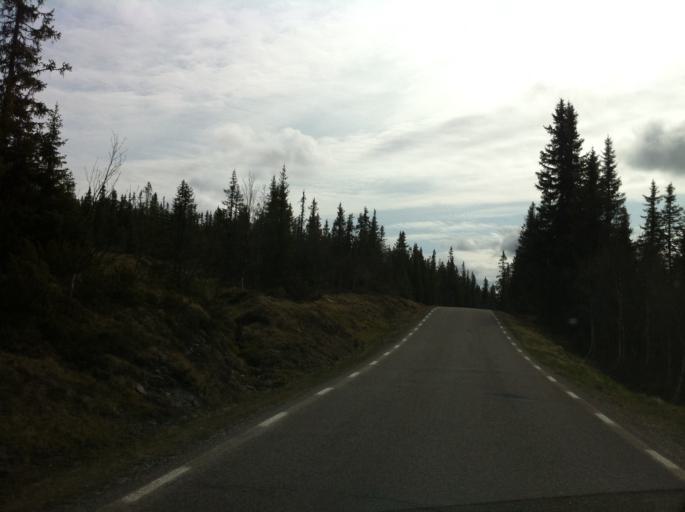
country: NO
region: Hedmark
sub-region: Engerdal
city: Engerdal
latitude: 62.3014
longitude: 12.8018
